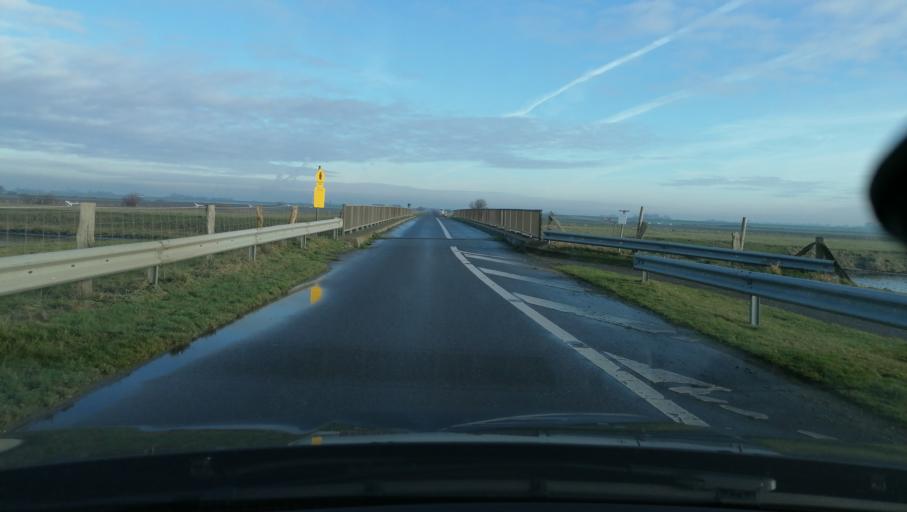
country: DE
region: Schleswig-Holstein
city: Friedrichsgabekoog
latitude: 54.1177
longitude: 8.9673
